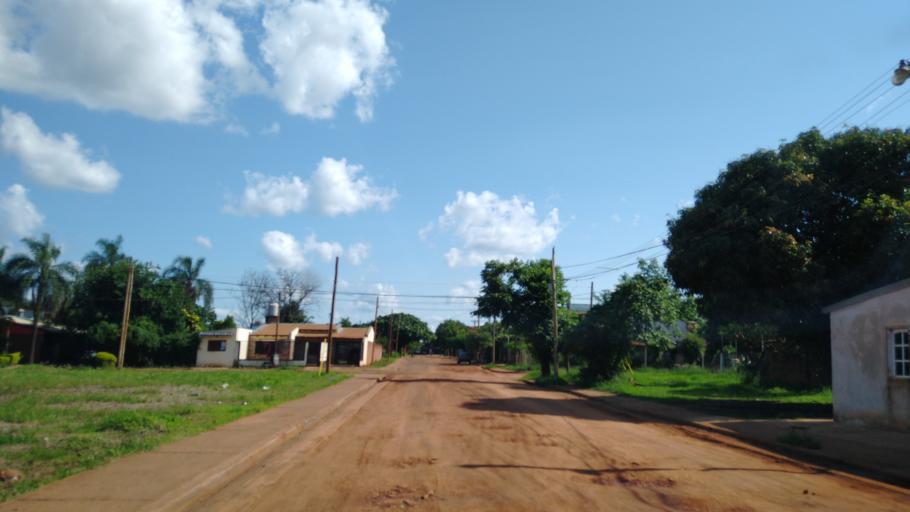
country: AR
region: Misiones
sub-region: Departamento de Capital
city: Posadas
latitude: -27.4041
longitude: -55.9171
